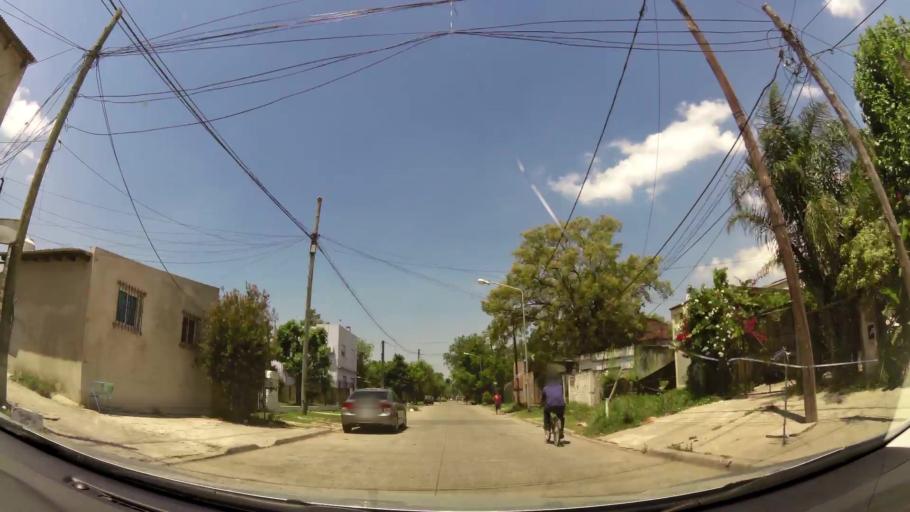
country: AR
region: Buenos Aires
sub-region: Partido de Tigre
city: Tigre
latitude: -34.4085
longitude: -58.5992
